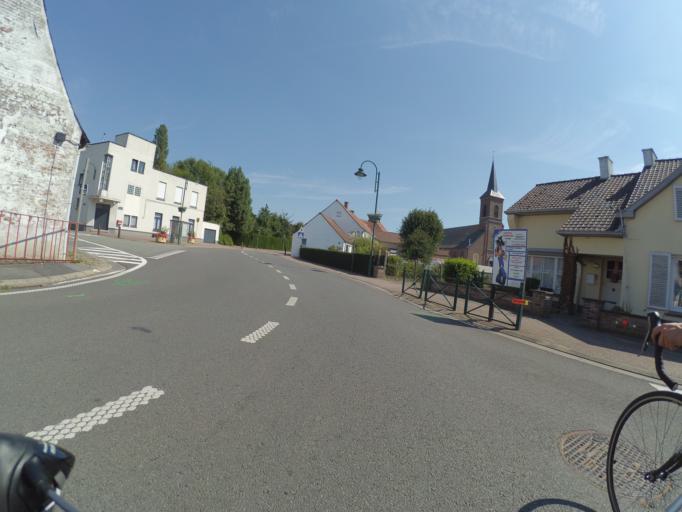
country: BE
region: Wallonia
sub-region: Province du Hainaut
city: Celles
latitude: 50.7481
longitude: 3.4804
